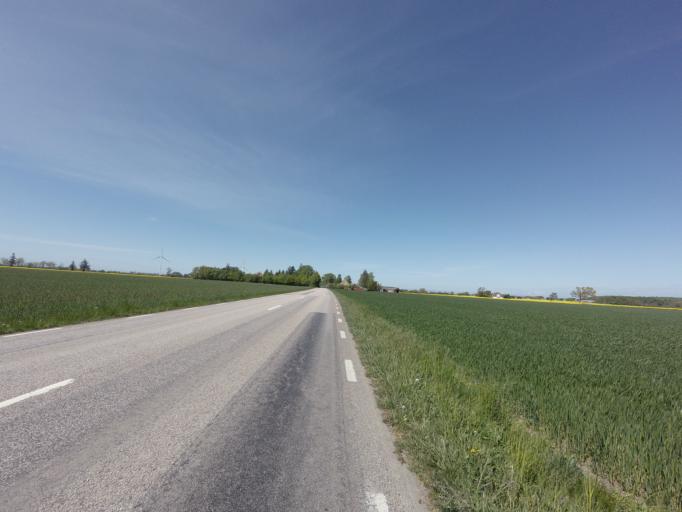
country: SE
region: Skane
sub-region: Helsingborg
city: Odakra
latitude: 56.1410
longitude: 12.6862
